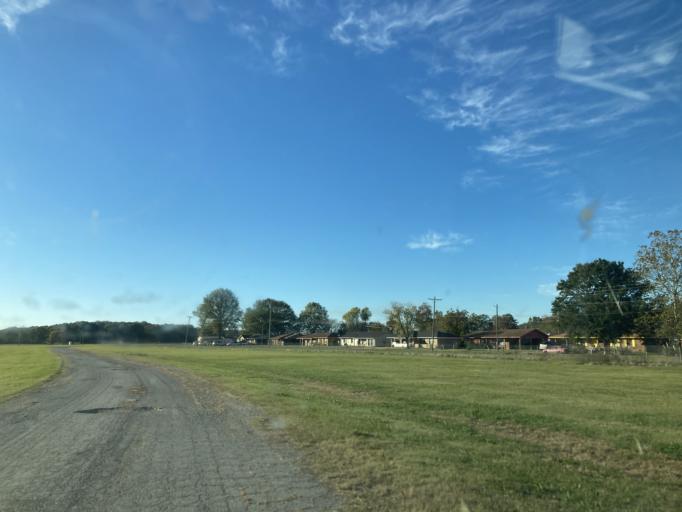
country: US
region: Mississippi
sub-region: Yazoo County
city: Yazoo City
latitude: 32.8795
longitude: -90.4168
